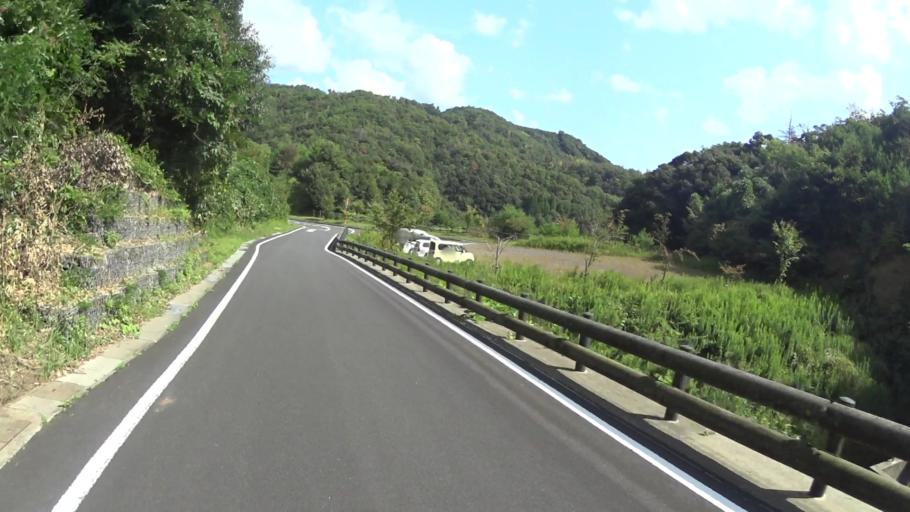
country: JP
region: Kyoto
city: Miyazu
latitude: 35.6262
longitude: 135.2349
